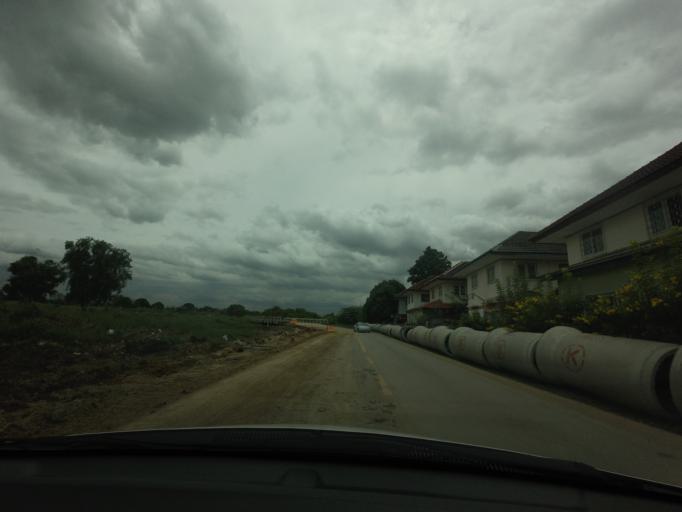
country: TH
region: Bangkok
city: Min Buri
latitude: 13.7787
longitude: 100.7613
